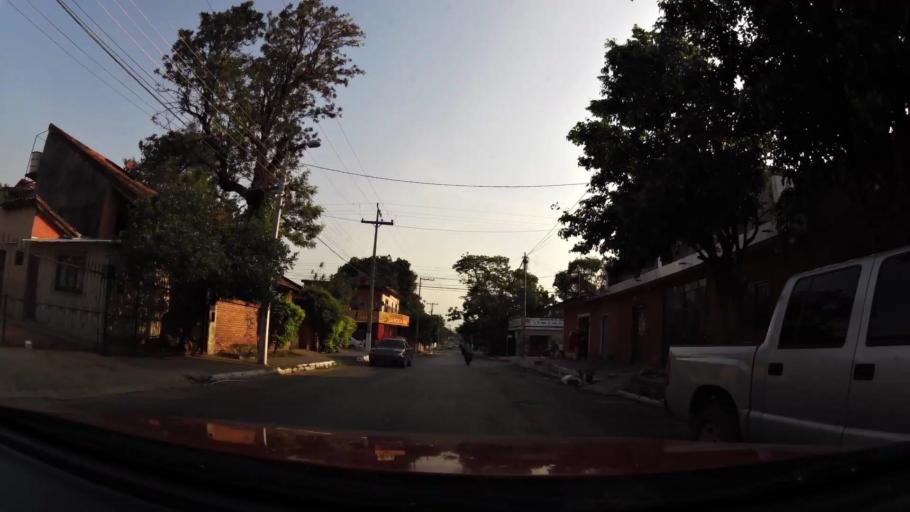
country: PY
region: Central
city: Lambare
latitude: -25.3540
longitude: -57.5969
